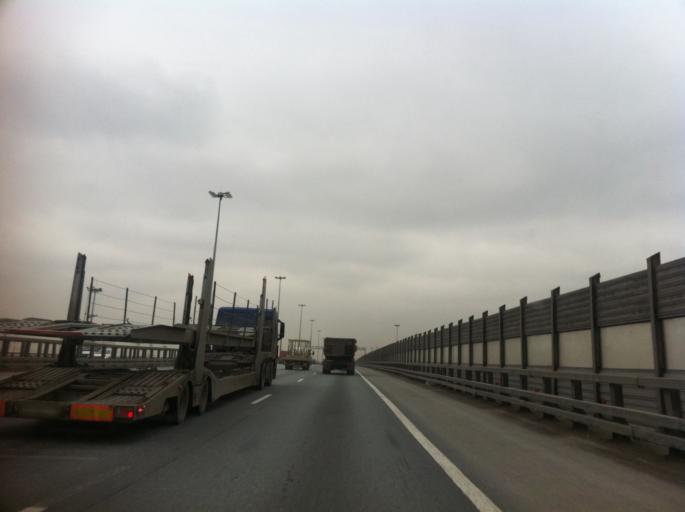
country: RU
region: St.-Petersburg
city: Obukhovo
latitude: 59.8334
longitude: 30.4458
